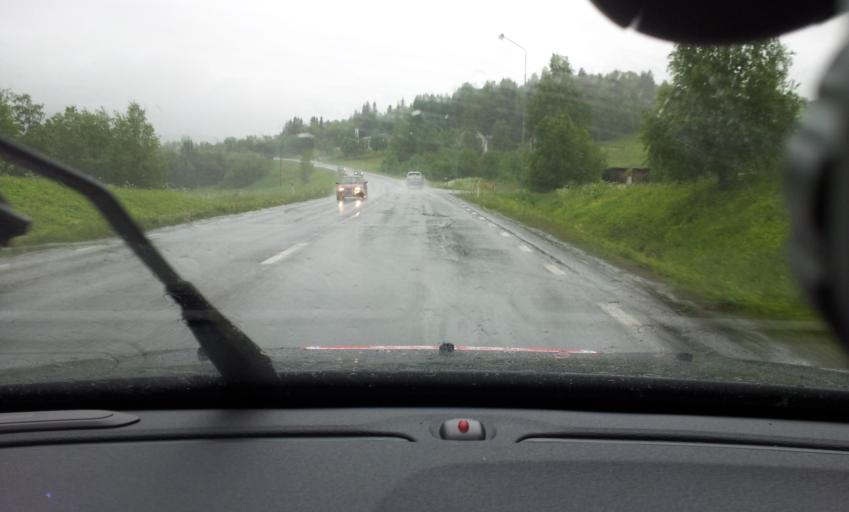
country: SE
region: Jaemtland
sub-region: Are Kommun
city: Are
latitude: 63.3398
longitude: 13.2066
